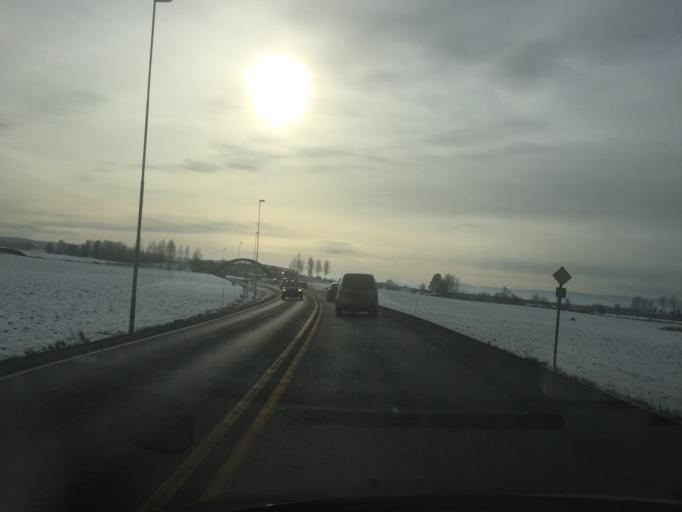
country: NO
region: Hedmark
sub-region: Loten
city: Loten
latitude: 60.8017
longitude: 11.2915
